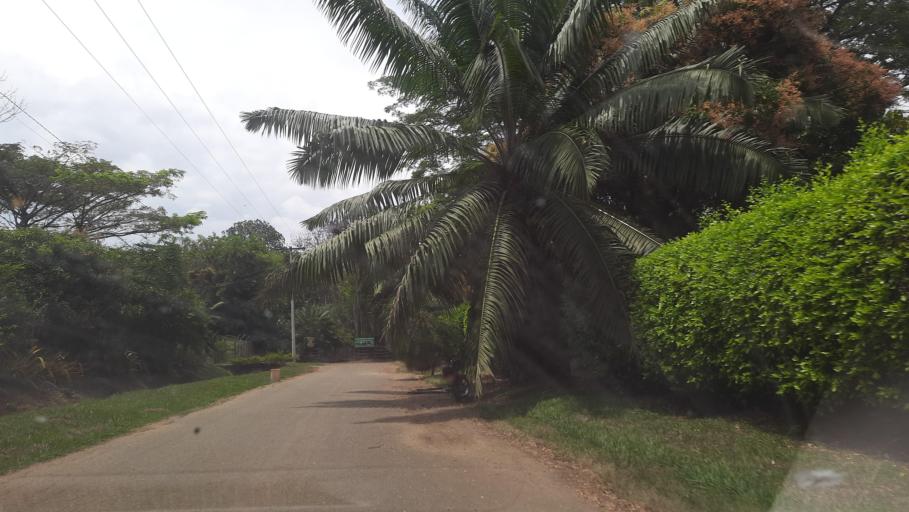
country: CO
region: Valle del Cauca
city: Jamundi
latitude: 3.2675
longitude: -76.5106
